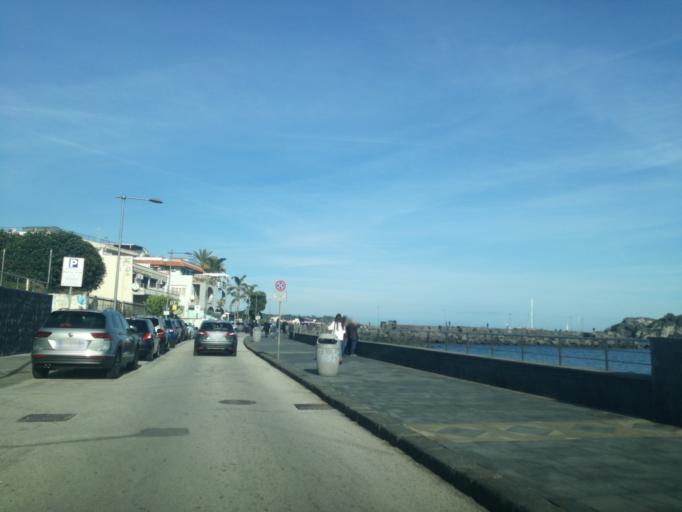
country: IT
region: Sicily
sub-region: Catania
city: Acitrezza
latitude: 37.5598
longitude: 15.1610
